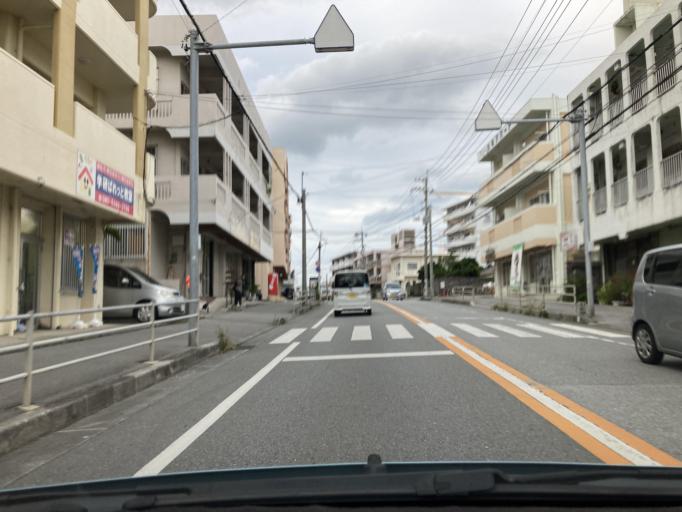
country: JP
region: Okinawa
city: Tomigusuku
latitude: 26.1840
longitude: 127.6821
